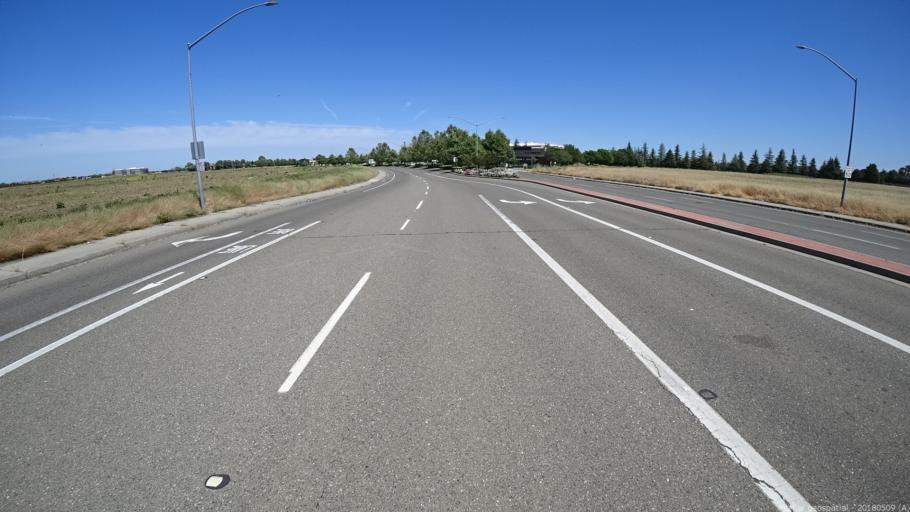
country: US
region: California
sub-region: Yolo County
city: West Sacramento
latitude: 38.6436
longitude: -121.5195
